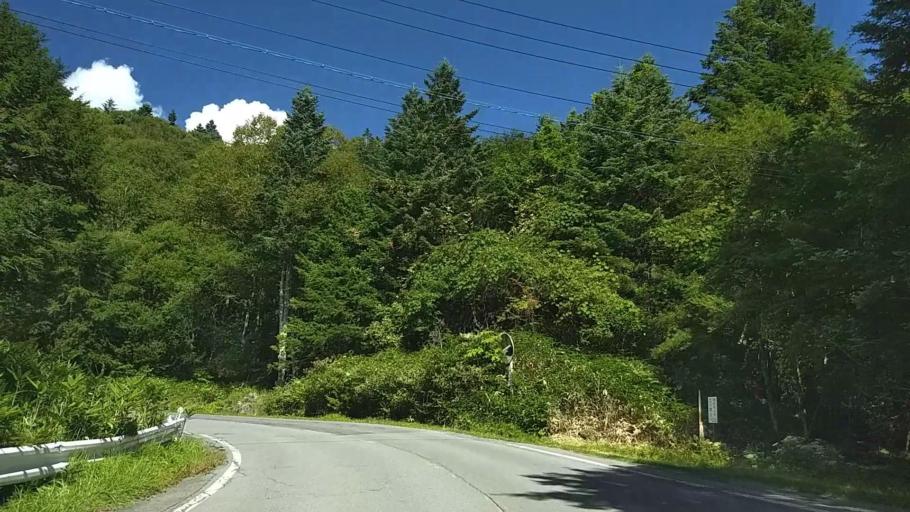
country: JP
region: Nagano
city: Chino
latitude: 36.0794
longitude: 138.2934
